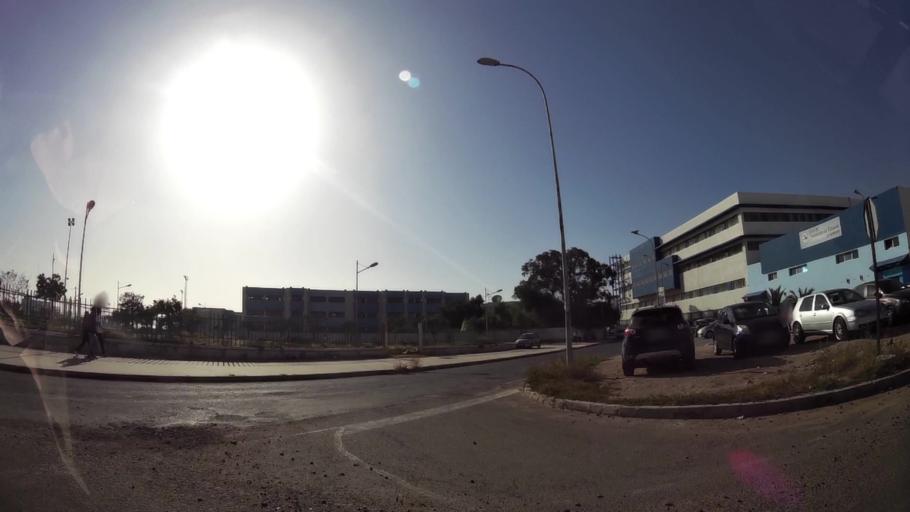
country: MA
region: Souss-Massa-Draa
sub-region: Agadir-Ida-ou-Tnan
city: Agadir
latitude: 30.4239
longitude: -9.5778
